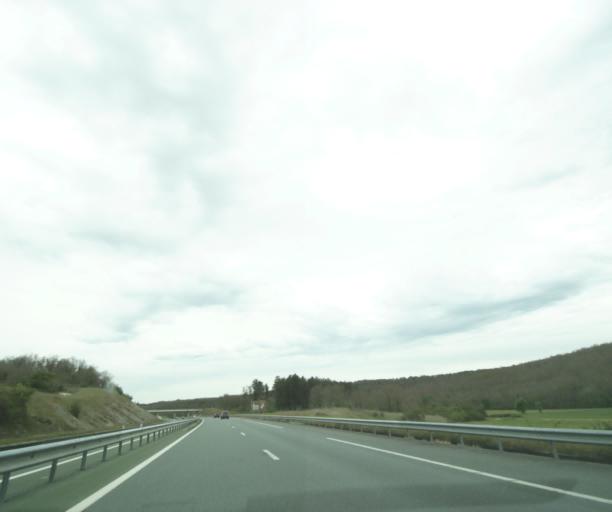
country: FR
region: Midi-Pyrenees
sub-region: Departement du Lot
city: Le Vigan
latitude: 44.7841
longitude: 1.5302
